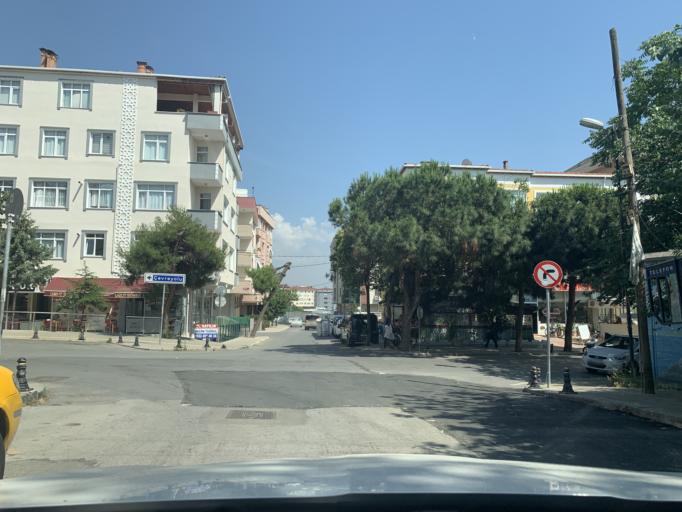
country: TR
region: Istanbul
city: Pendik
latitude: 40.8575
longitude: 29.2801
